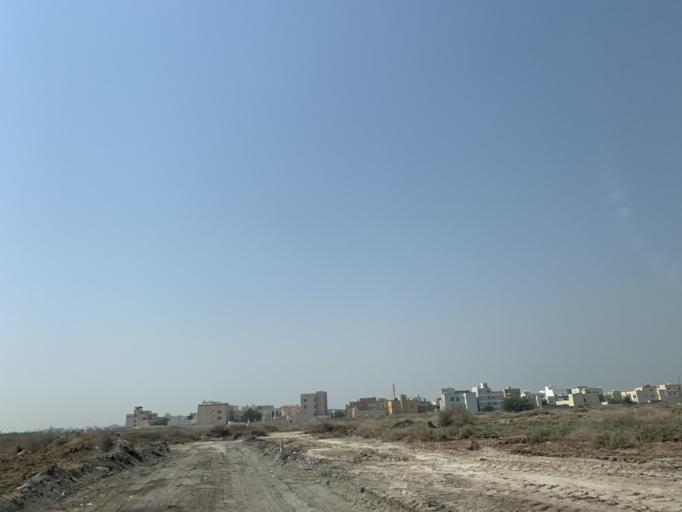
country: BH
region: Manama
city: Jidd Hafs
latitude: 26.2010
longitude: 50.5153
